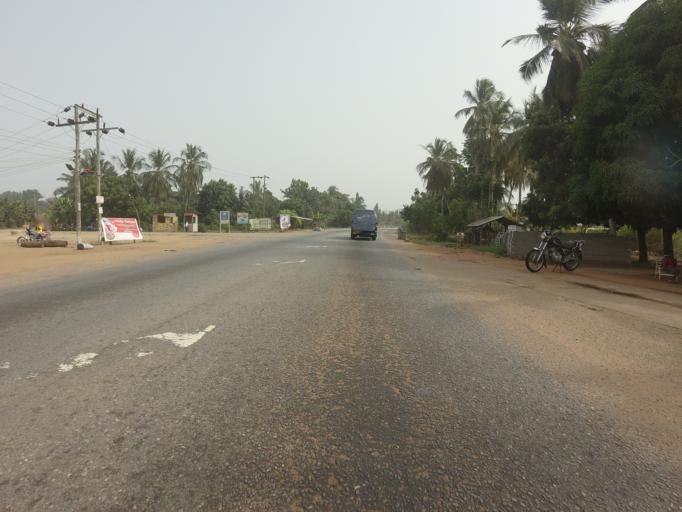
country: GH
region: Volta
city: Anloga
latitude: 6.0038
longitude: 0.5619
